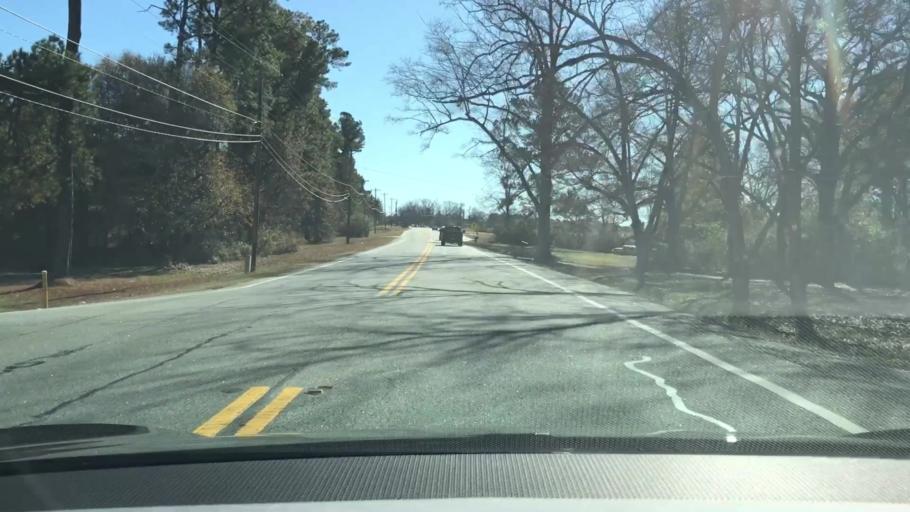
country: US
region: Georgia
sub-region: Walton County
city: Monroe
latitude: 33.8202
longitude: -83.7319
